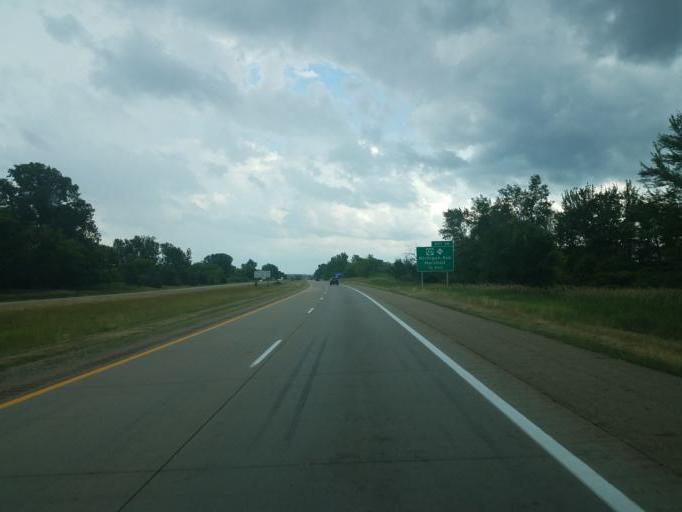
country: US
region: Michigan
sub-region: Calhoun County
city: Marshall
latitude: 42.2867
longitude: -84.9977
